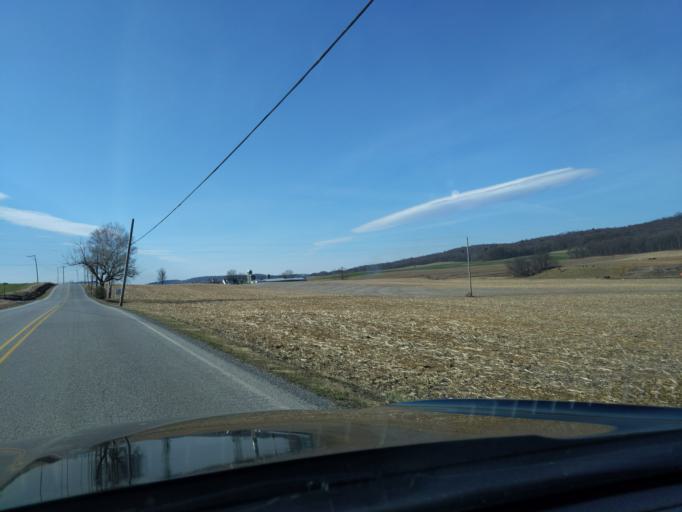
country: US
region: Pennsylvania
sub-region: Blair County
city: Martinsburg
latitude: 40.3387
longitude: -78.2616
